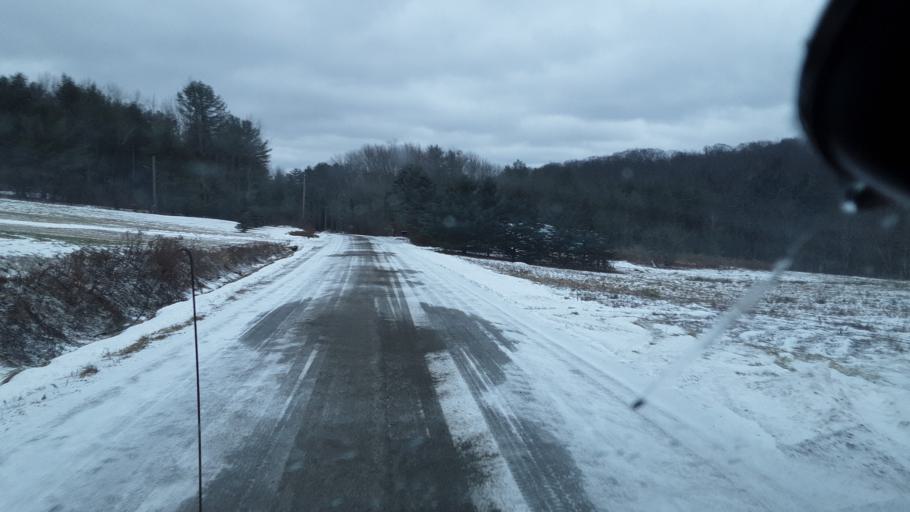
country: US
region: New York
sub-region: Allegany County
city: Friendship
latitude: 42.2305
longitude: -78.1339
